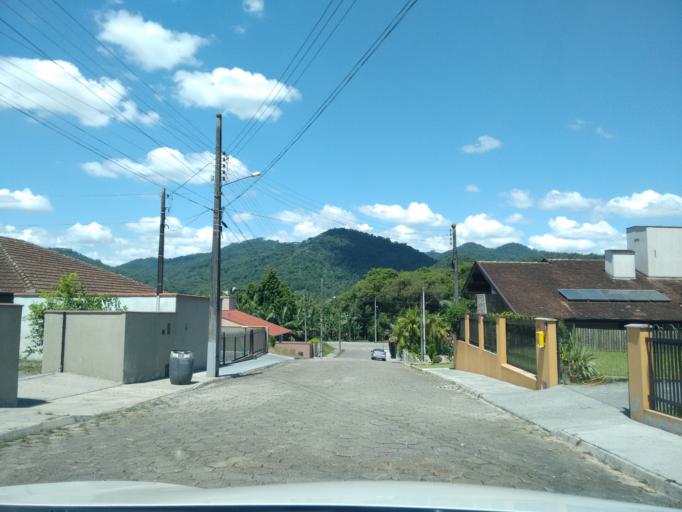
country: BR
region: Santa Catarina
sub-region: Pomerode
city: Pomerode
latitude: -26.7514
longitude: -49.1762
